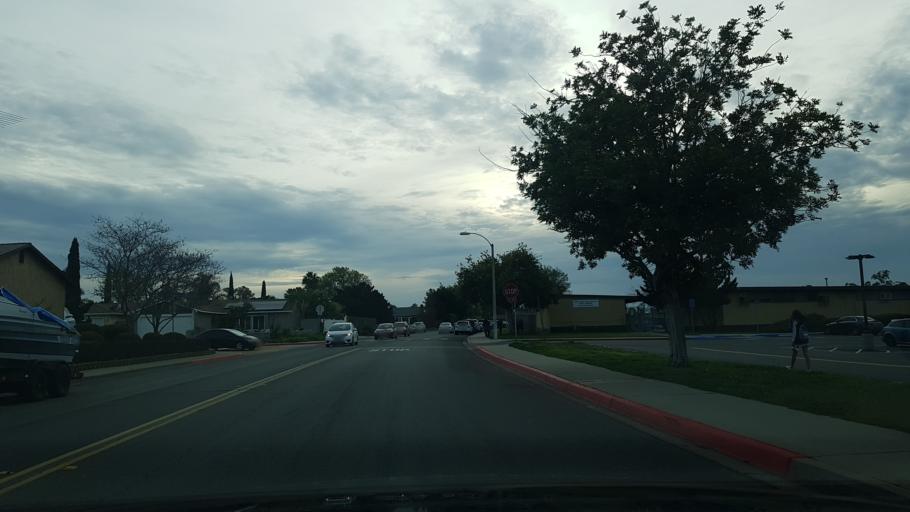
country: US
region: California
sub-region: San Diego County
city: Fairbanks Ranch
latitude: 32.9089
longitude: -117.1406
